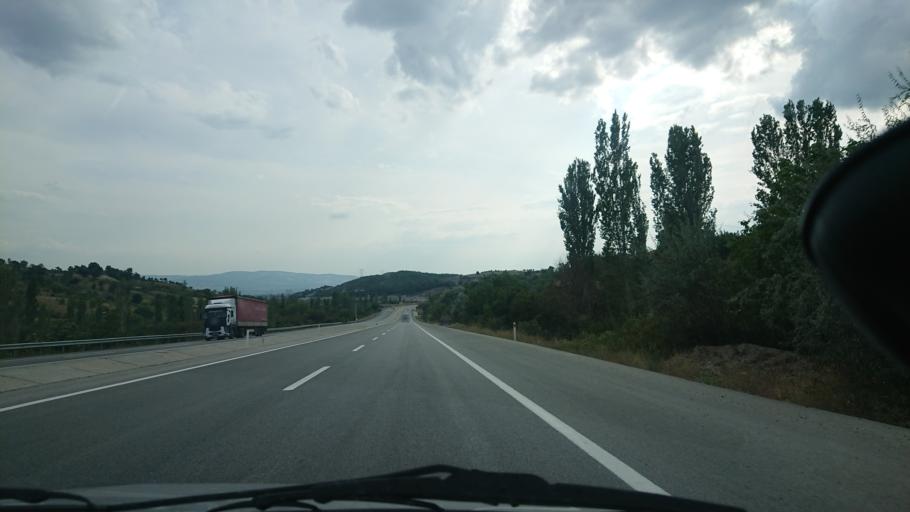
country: TR
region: Kuetahya
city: Gediz
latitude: 39.0407
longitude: 29.4238
